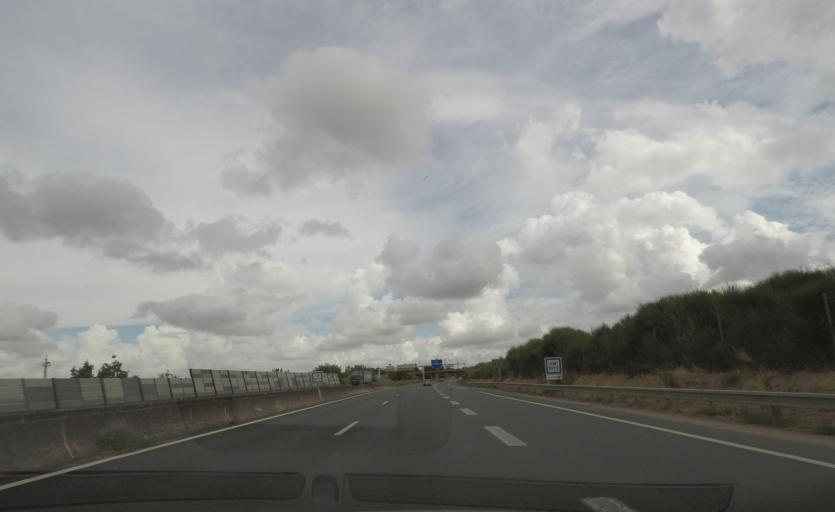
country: FR
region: Pays de la Loire
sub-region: Departement de Maine-et-Loire
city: Angers
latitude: 47.4636
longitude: -0.5170
